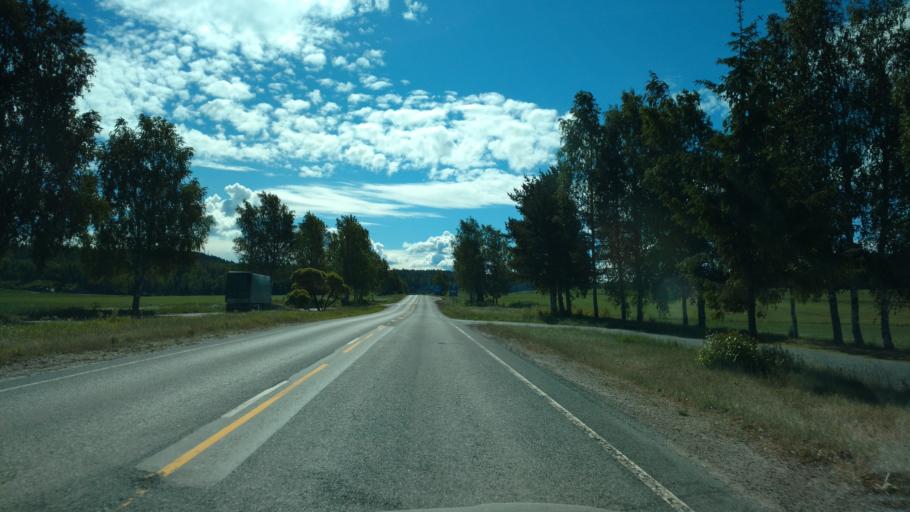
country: FI
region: Varsinais-Suomi
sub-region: Salo
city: Muurla
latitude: 60.3774
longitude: 23.3049
